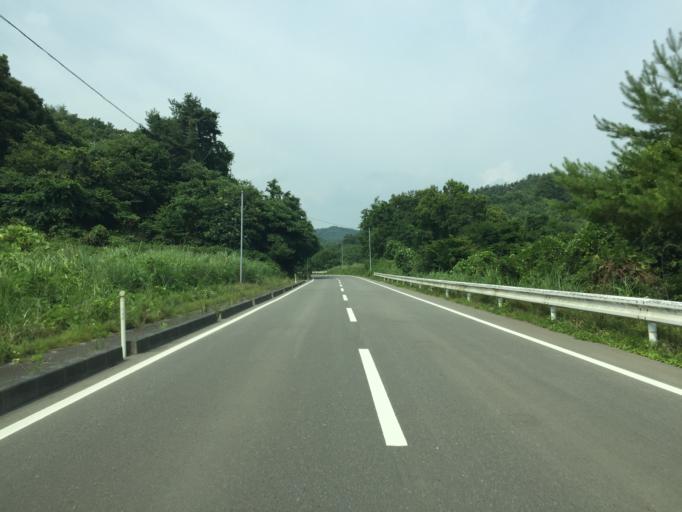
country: JP
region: Fukushima
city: Funehikimachi-funehiki
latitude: 37.4648
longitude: 140.7555
